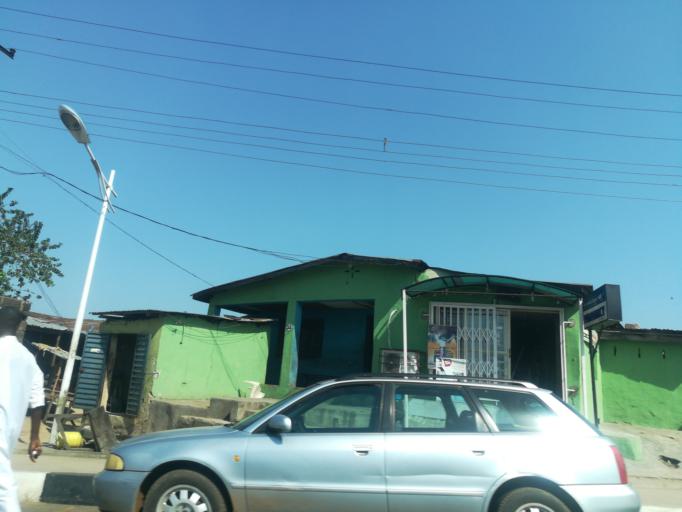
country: NG
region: Ogun
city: Abeokuta
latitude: 7.1430
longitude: 3.3307
